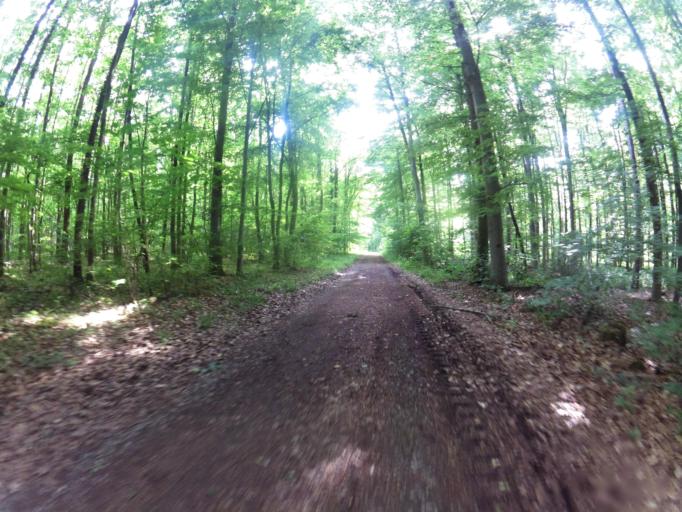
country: DE
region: Bavaria
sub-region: Regierungsbezirk Unterfranken
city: Ochsenfurt
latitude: 49.6843
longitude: 10.0660
